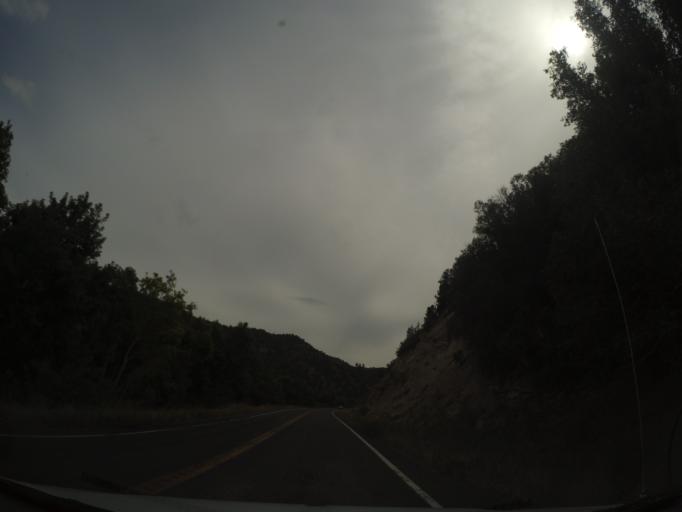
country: US
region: Utah
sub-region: Kane County
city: Kanab
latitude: 37.3556
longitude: -112.5988
